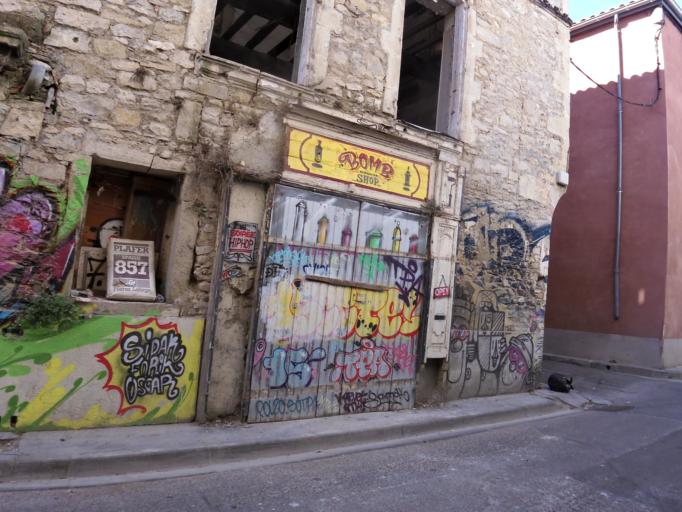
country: FR
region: Languedoc-Roussillon
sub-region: Departement du Gard
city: Nimes
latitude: 43.8419
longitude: 4.3604
